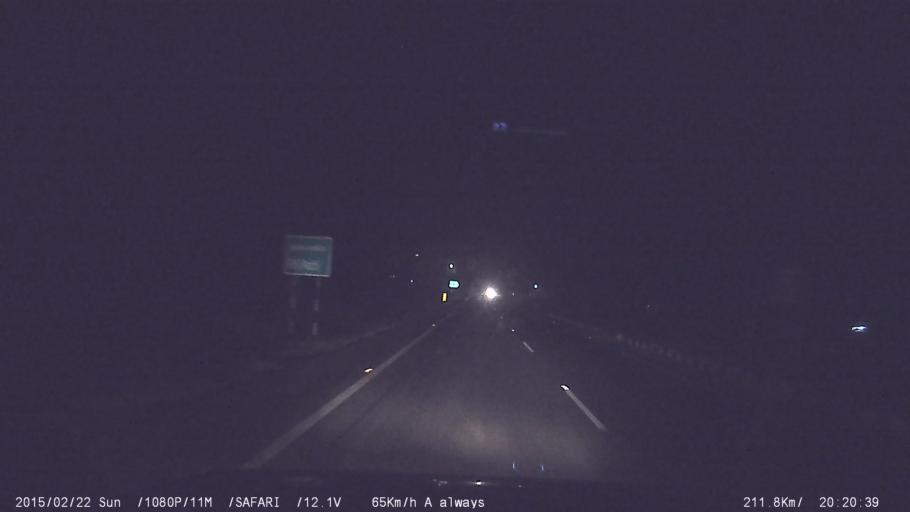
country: IN
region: Tamil Nadu
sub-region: Dindigul
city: Nilakottai
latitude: 10.2849
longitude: 77.8743
